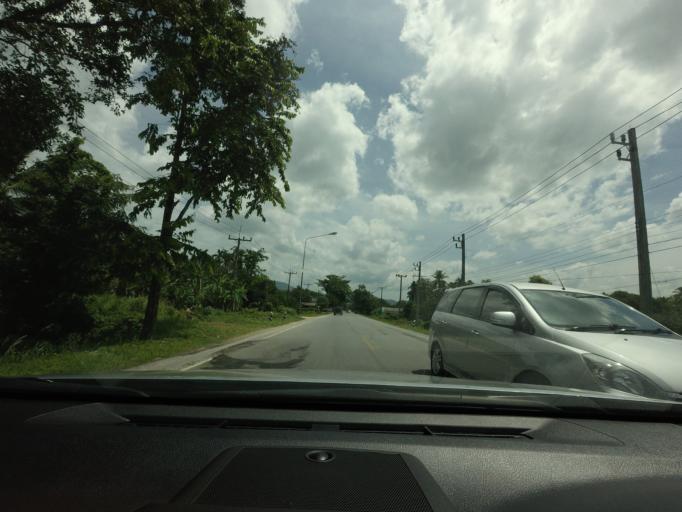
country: TH
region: Yala
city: Raman
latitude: 6.4638
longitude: 101.3791
